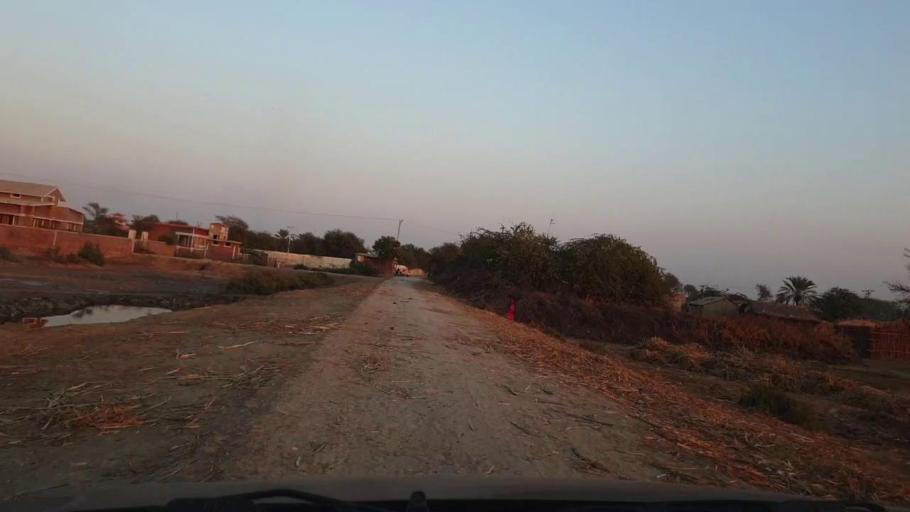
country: PK
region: Sindh
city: Jhol
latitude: 25.9295
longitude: 68.9744
